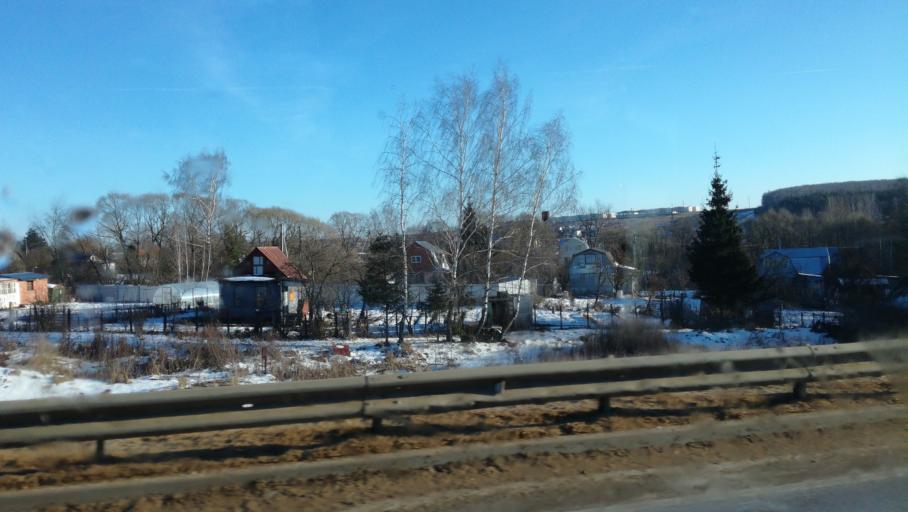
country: RU
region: Tula
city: Barsuki
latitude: 54.1765
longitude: 37.4527
